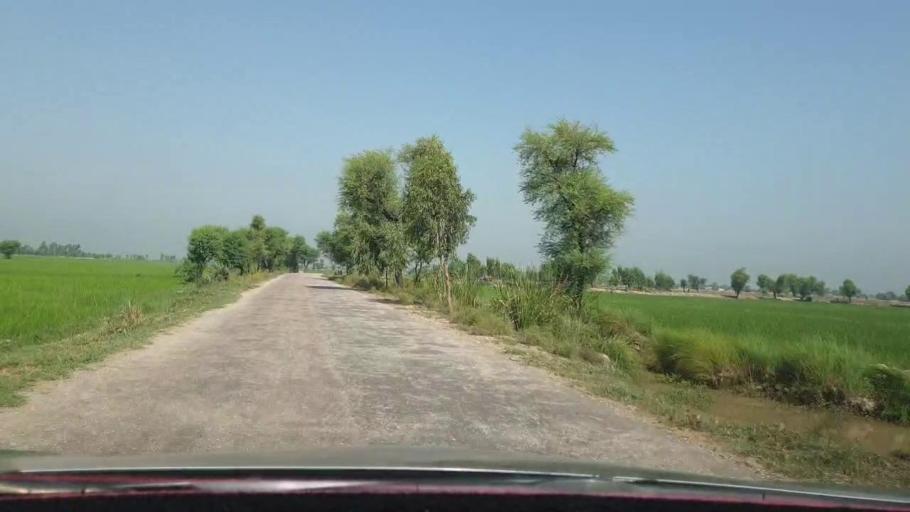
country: PK
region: Sindh
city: Warah
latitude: 27.4715
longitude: 67.8327
